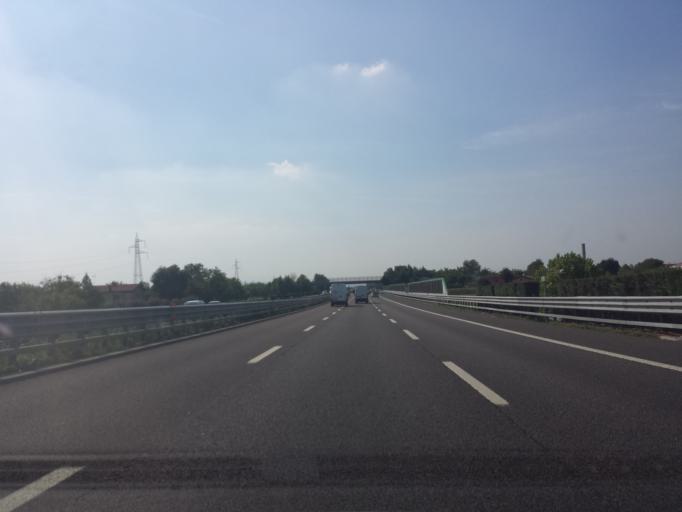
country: IT
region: Veneto
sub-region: Provincia di Padova
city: Villaguattera
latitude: 45.4518
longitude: 11.8236
